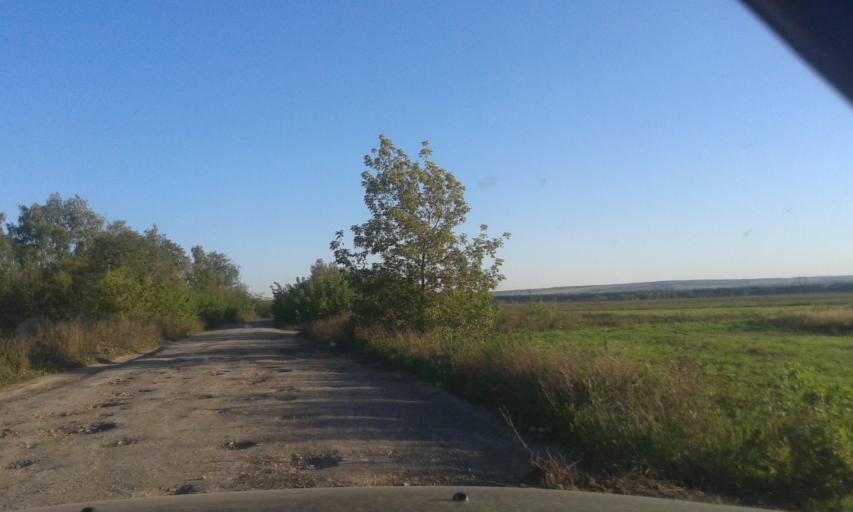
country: RU
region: Tula
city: Krapivna
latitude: 54.1336
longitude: 37.1571
